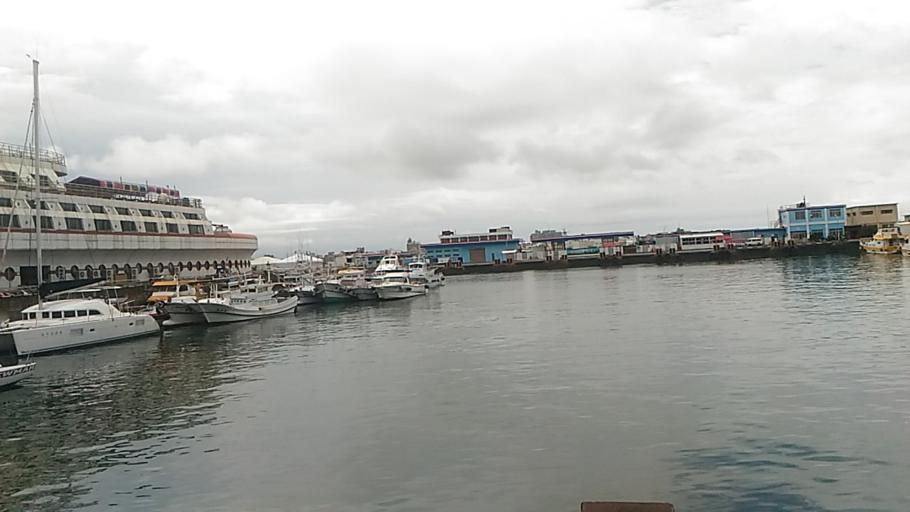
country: TW
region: Taiwan
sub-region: Penghu
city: Ma-kung
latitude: 23.5657
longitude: 119.5692
